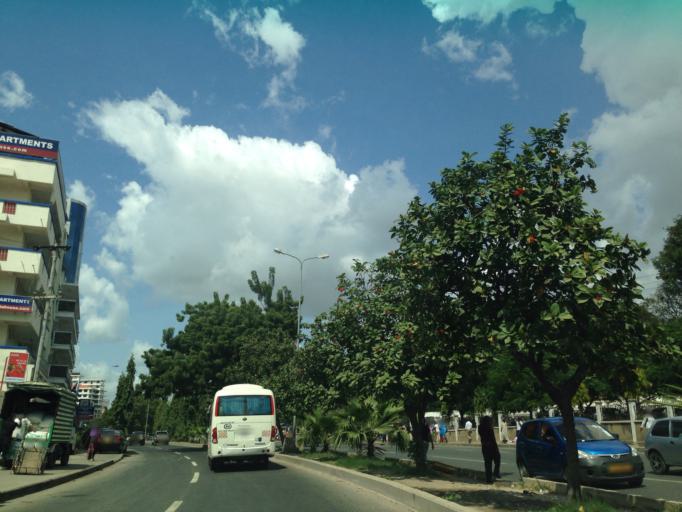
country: TZ
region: Dar es Salaam
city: Dar es Salaam
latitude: -6.8172
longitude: 39.2801
